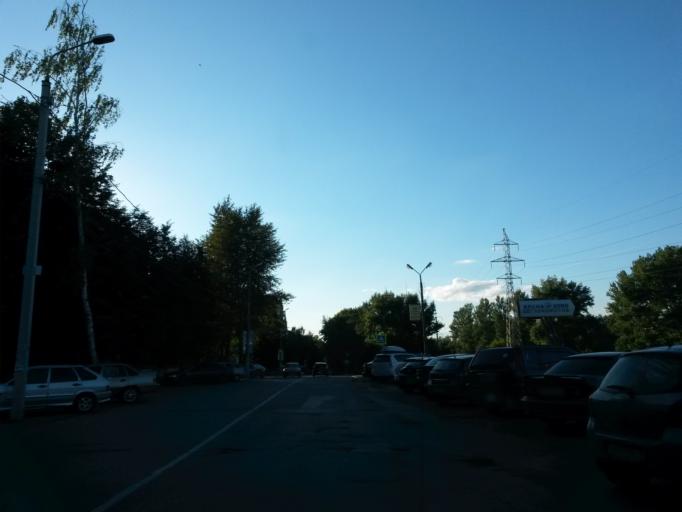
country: RU
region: Jaroslavl
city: Yaroslavl
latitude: 57.5849
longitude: 39.8437
